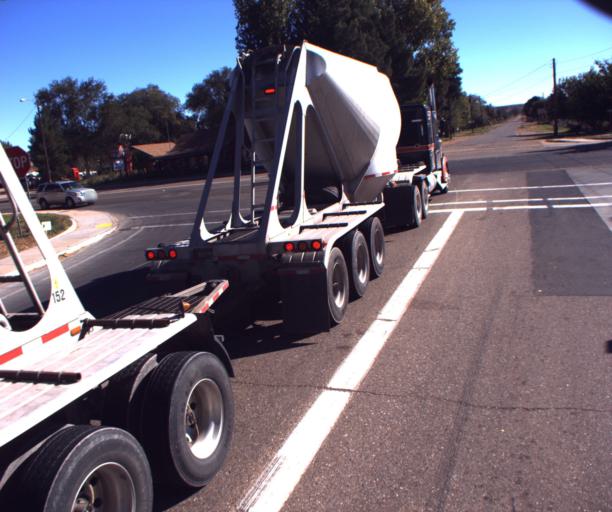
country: US
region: Arizona
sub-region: Coconino County
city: Fredonia
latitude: 36.9456
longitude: -112.5268
